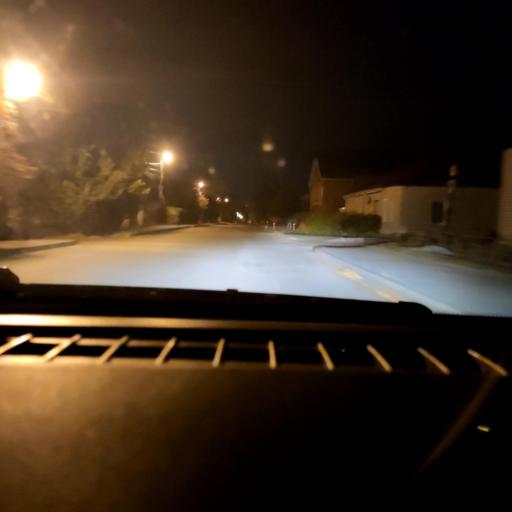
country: RU
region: Voronezj
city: Voronezh
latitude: 51.6795
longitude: 39.1391
